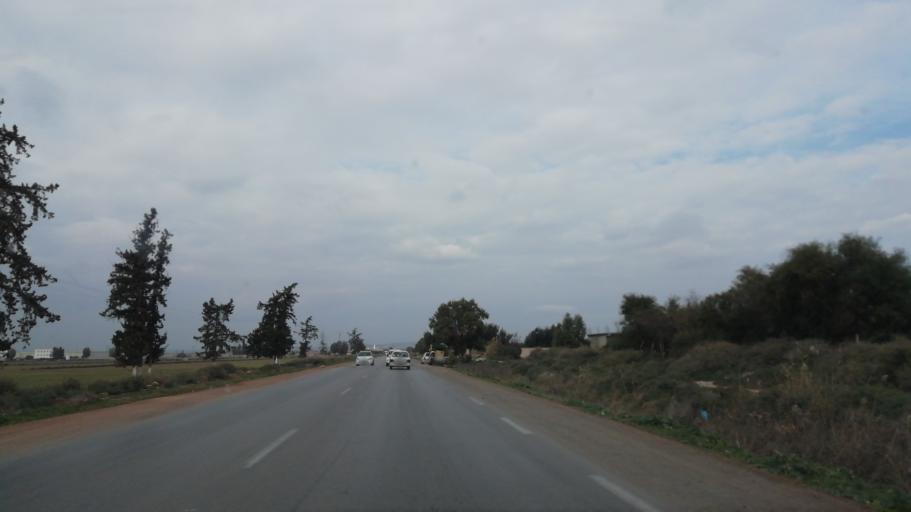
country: DZ
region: Mostaganem
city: Mostaganem
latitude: 35.6877
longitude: 0.0563
